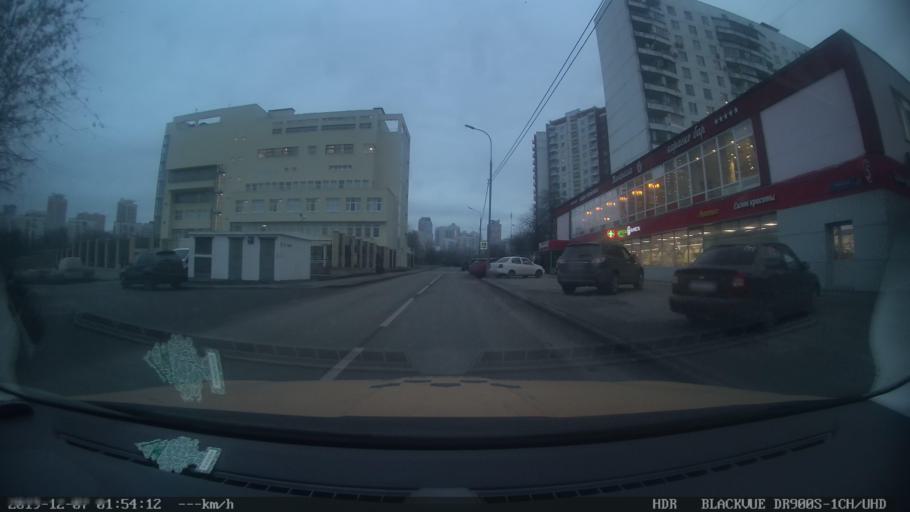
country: RU
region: Moscow
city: Troparevo
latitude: 55.6668
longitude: 37.4964
